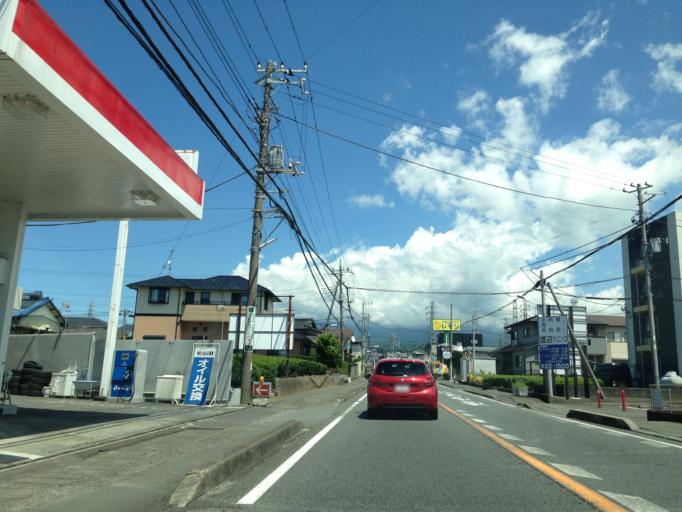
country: JP
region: Shizuoka
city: Fuji
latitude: 35.1717
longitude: 138.6898
